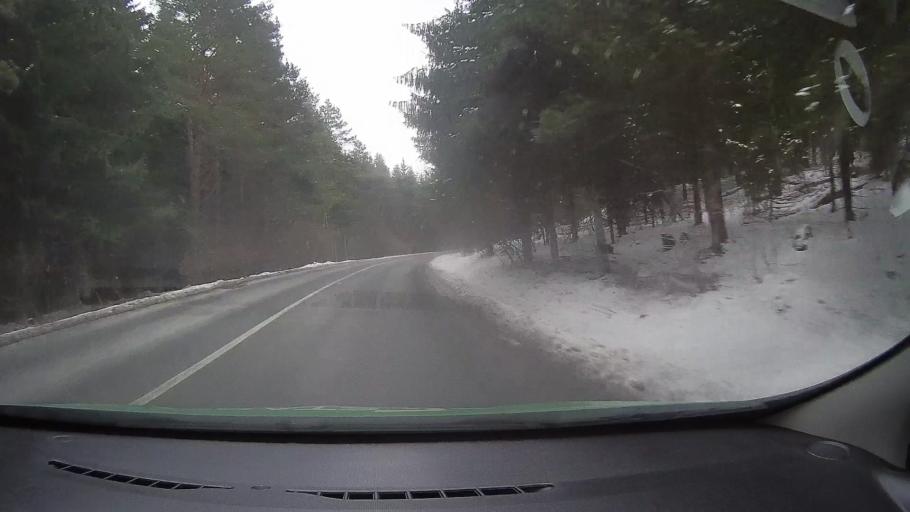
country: RO
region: Brasov
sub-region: Oras Predeal
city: Predeal
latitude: 45.5198
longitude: 25.5028
